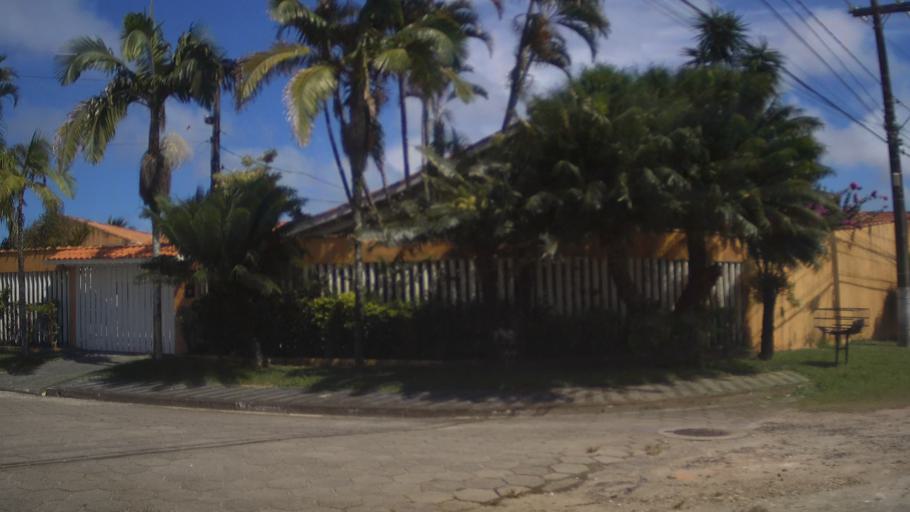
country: BR
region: Sao Paulo
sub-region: Itanhaem
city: Itanhaem
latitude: -24.1470
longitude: -46.7213
